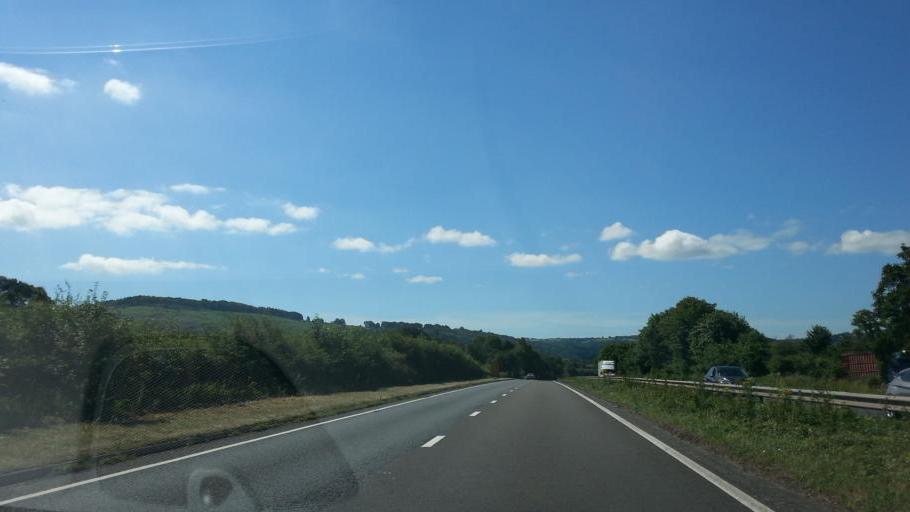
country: GB
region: England
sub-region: Herefordshire
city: Marstow
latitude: 51.8761
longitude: -2.6303
